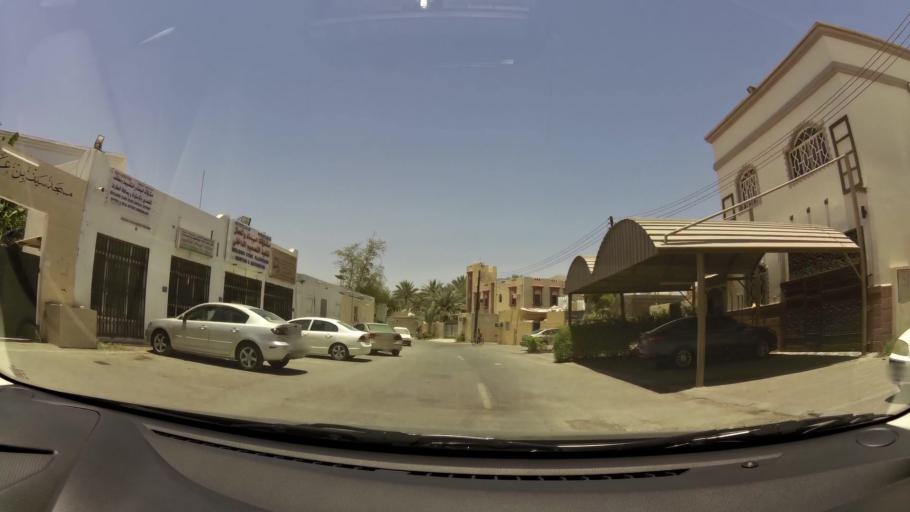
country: OM
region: Muhafazat Masqat
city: As Sib al Jadidah
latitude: 23.6323
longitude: 58.2341
